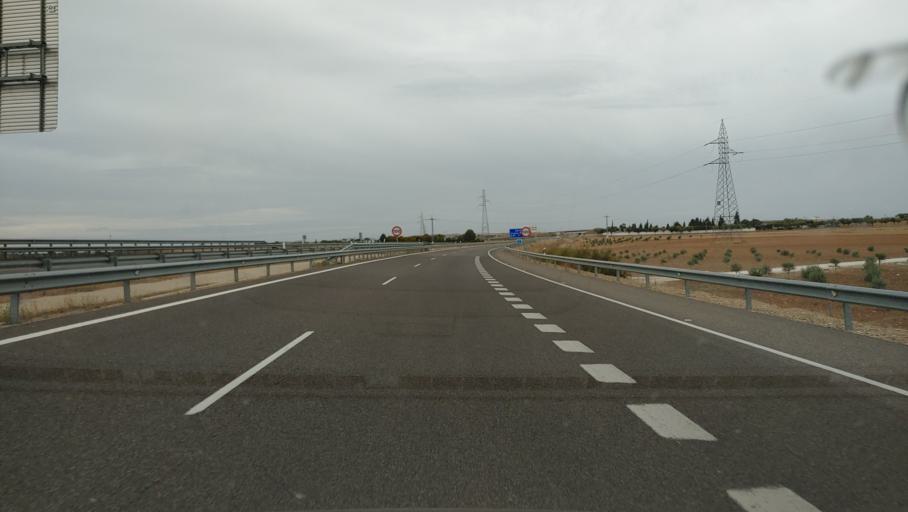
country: ES
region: Castille-La Mancha
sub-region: Provincia de Ciudad Real
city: Miguelturra
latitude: 38.9471
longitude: -3.8805
